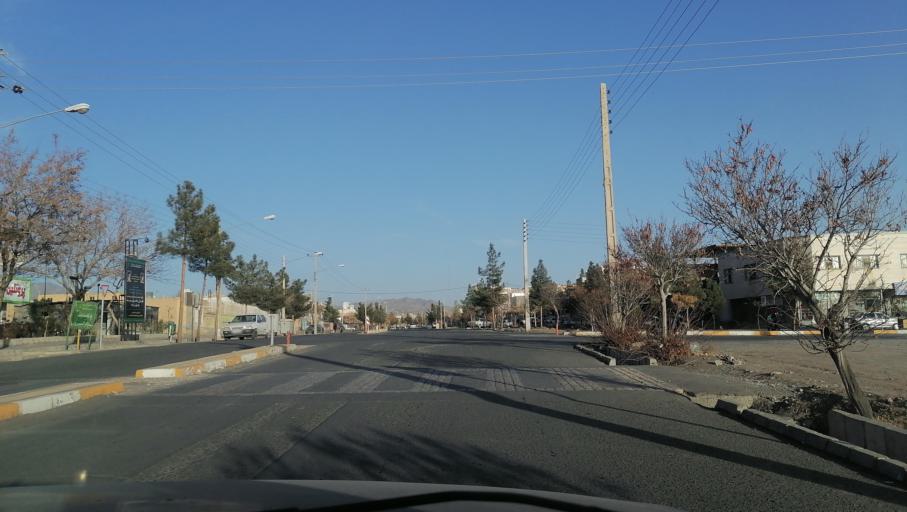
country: IR
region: Razavi Khorasan
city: Sabzevar
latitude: 36.2849
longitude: 57.6744
